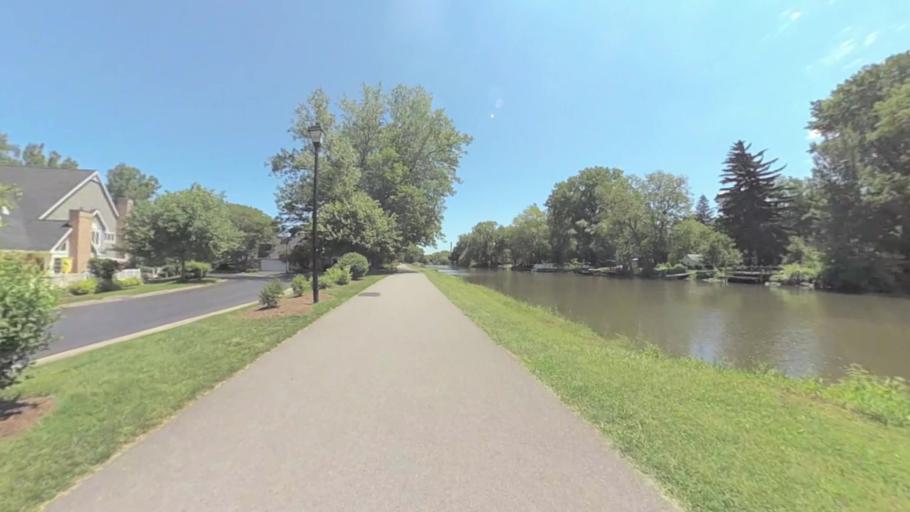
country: US
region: New York
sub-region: Monroe County
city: Fairport
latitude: 43.1037
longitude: -77.4528
